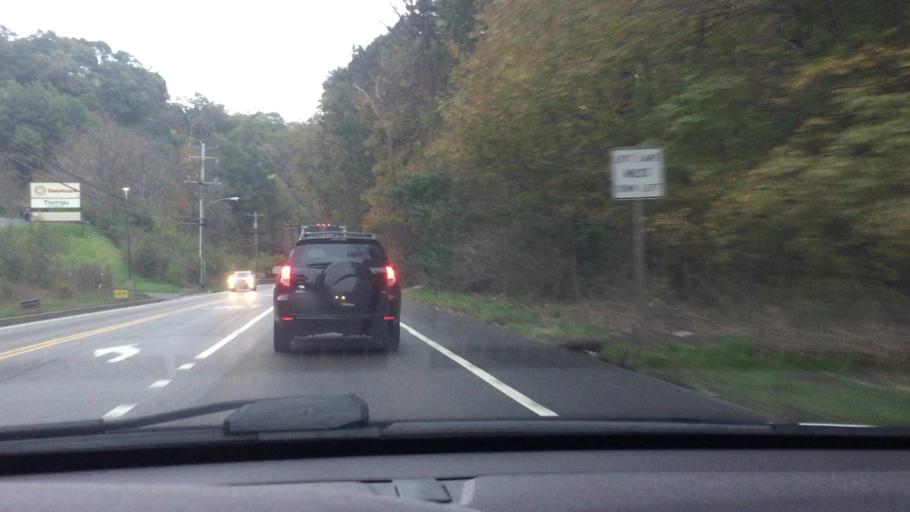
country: US
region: Pennsylvania
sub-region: Allegheny County
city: Ingram
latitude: 40.4477
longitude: -80.1033
